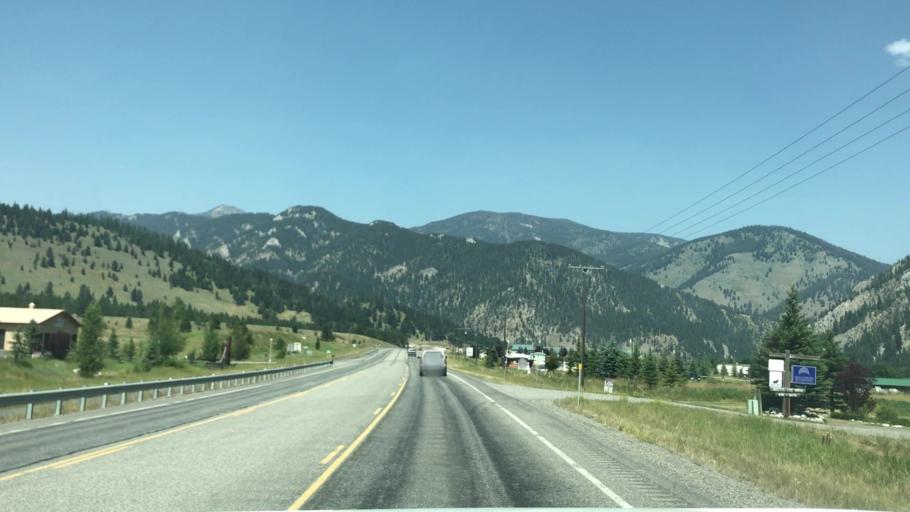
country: US
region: Montana
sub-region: Gallatin County
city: Big Sky
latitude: 45.2484
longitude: -111.2519
